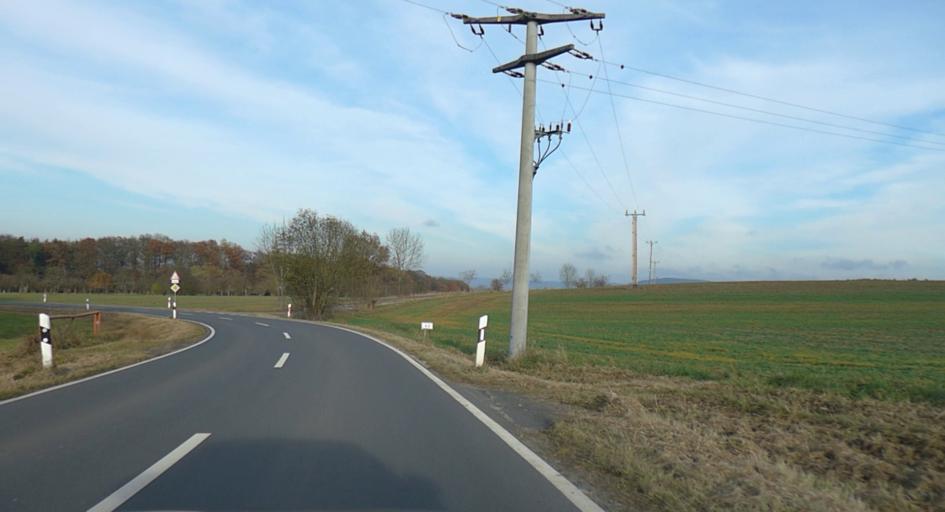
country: DE
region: Bavaria
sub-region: Regierungsbezirk Mittelfranken
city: Bubenreuth
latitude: 49.6190
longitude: 11.0308
